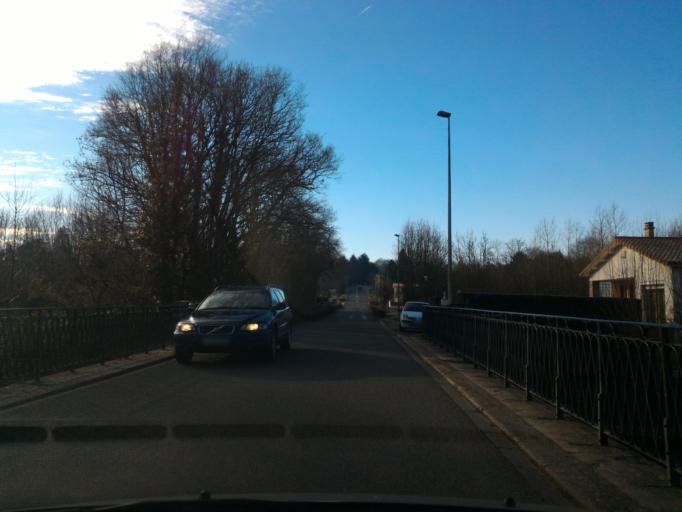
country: FR
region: Poitou-Charentes
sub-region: Departement de la Charente
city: Champagne-Mouton
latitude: 46.0255
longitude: 0.5102
